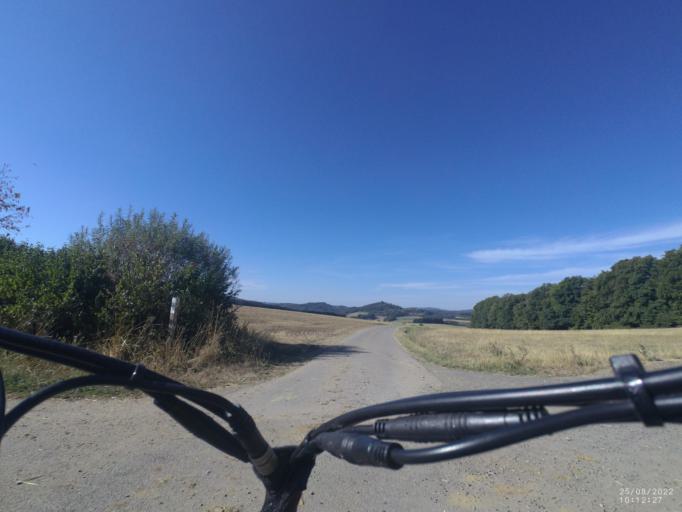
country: DE
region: Rheinland-Pfalz
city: Walsdorf
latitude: 50.2692
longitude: 6.7058
